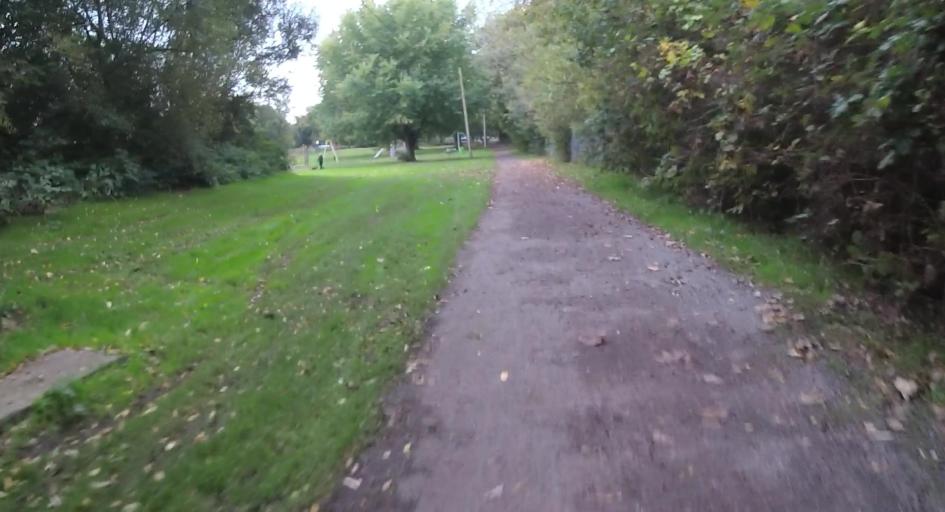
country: GB
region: England
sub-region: Bracknell Forest
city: Crowthorne
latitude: 51.3960
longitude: -0.7797
